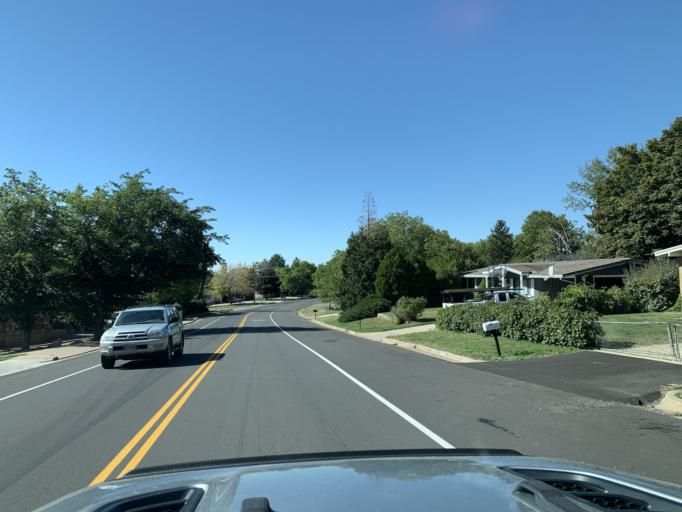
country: US
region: Utah
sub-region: Weber County
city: North Ogden
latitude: 41.3175
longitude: -111.9435
